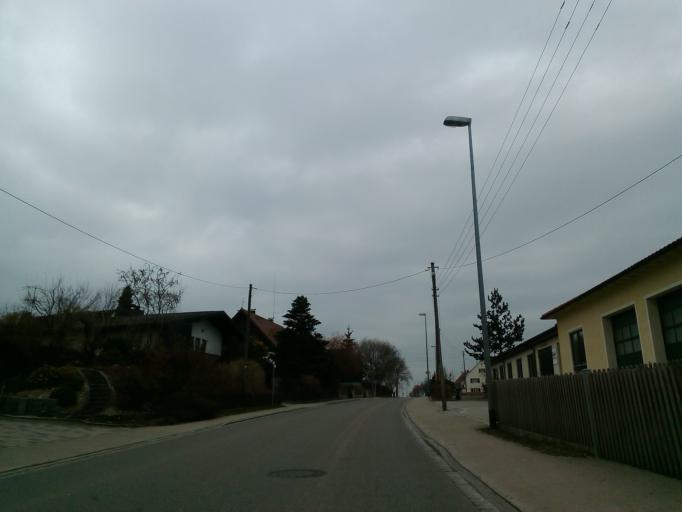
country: DE
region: Bavaria
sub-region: Swabia
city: Langenneufnach
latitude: 48.3058
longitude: 10.6096
